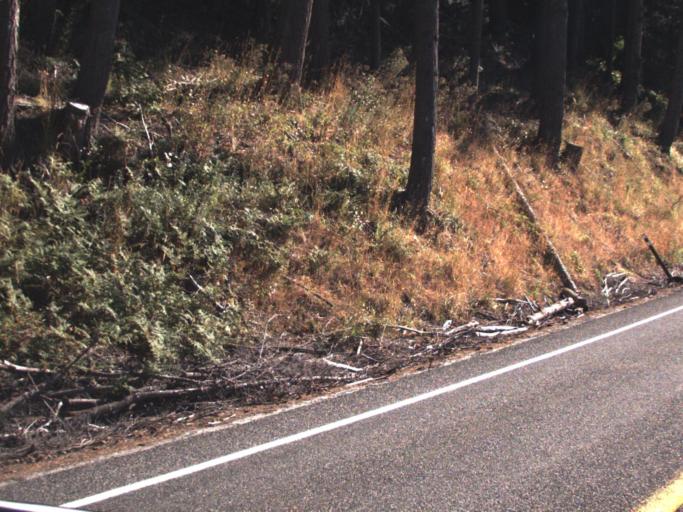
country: US
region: Washington
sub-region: King County
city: Enumclaw
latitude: 47.1527
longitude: -121.8494
